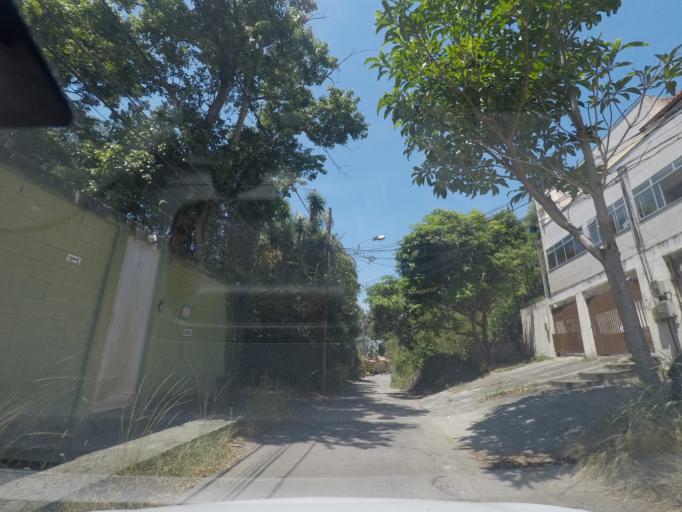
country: BR
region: Rio de Janeiro
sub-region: Niteroi
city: Niteroi
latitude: -22.9682
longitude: -43.0395
